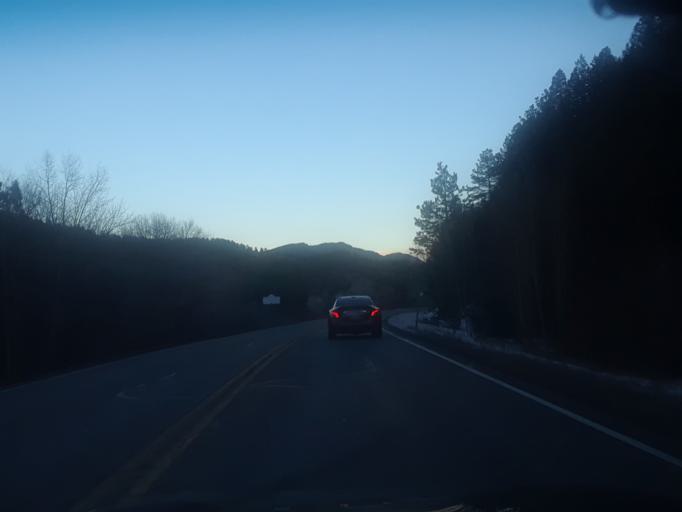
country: US
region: Colorado
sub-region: Clear Creek County
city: Georgetown
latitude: 39.4419
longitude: -105.6055
